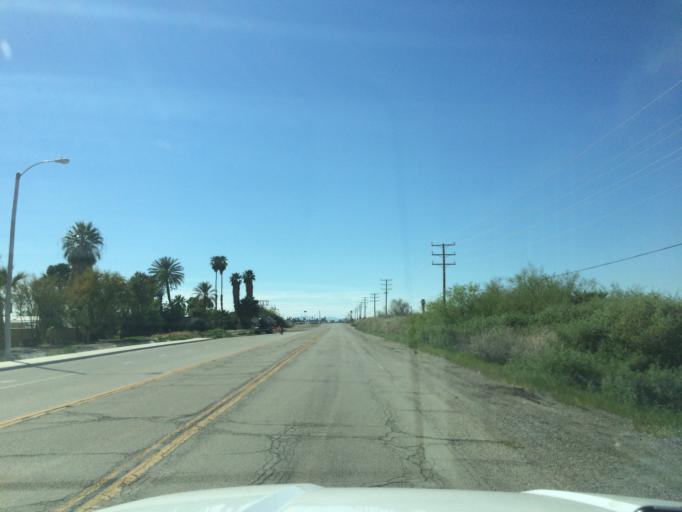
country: US
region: Arizona
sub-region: La Paz County
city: Ehrenberg
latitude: 33.6110
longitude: -114.5587
